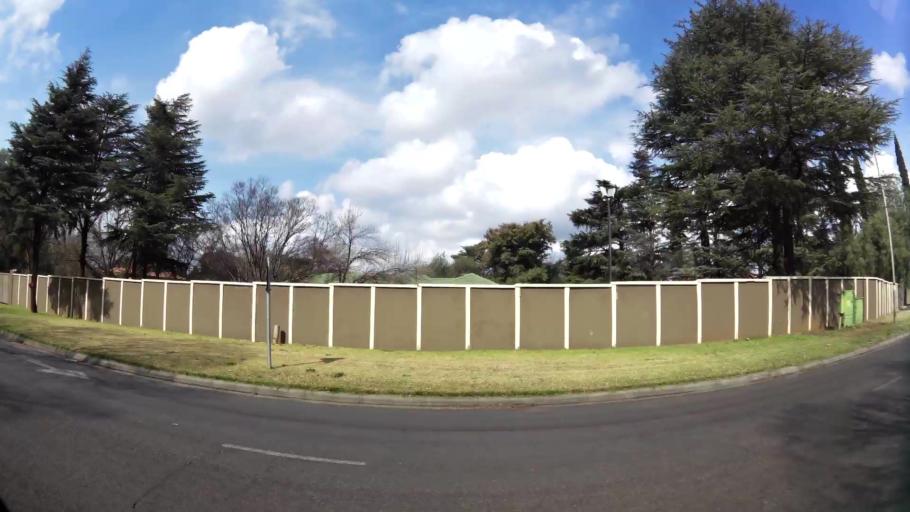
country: ZA
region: Gauteng
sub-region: Sedibeng District Municipality
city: Vanderbijlpark
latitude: -26.7336
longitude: 27.8277
